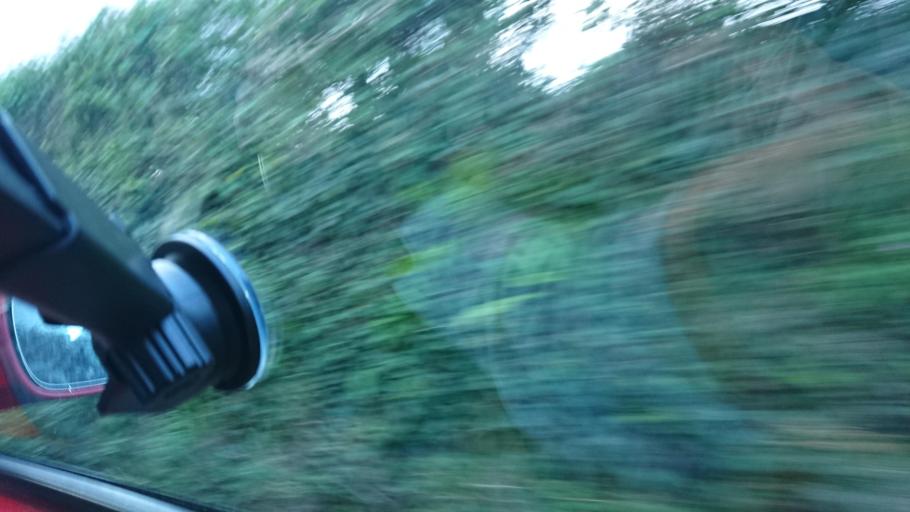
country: GB
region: England
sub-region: Cornwall
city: Looe
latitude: 50.3472
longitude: -4.4745
